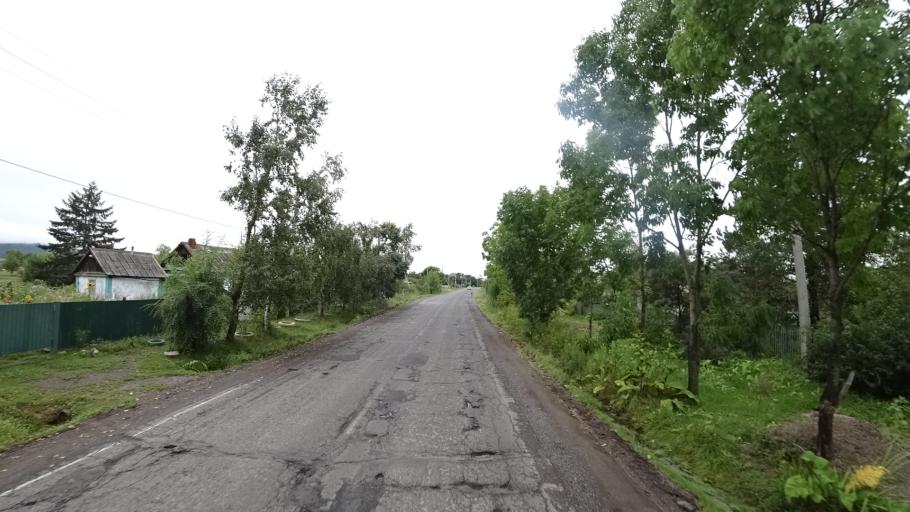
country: RU
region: Primorskiy
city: Monastyrishche
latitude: 44.1910
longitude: 132.4859
